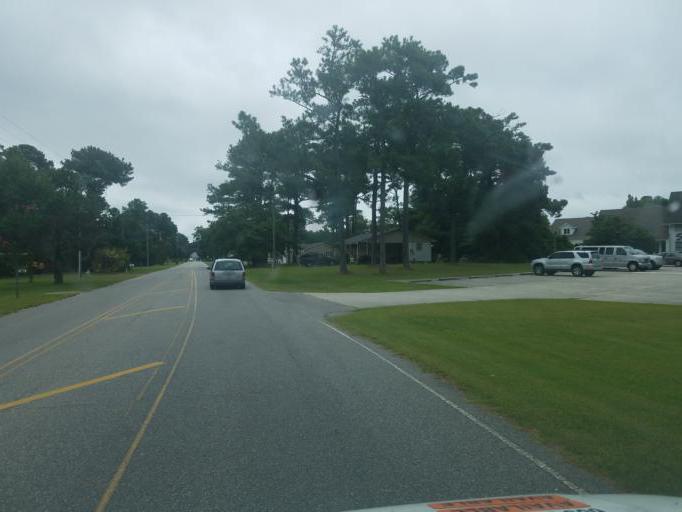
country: US
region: North Carolina
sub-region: Dare County
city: Wanchese
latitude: 35.8490
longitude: -75.6415
